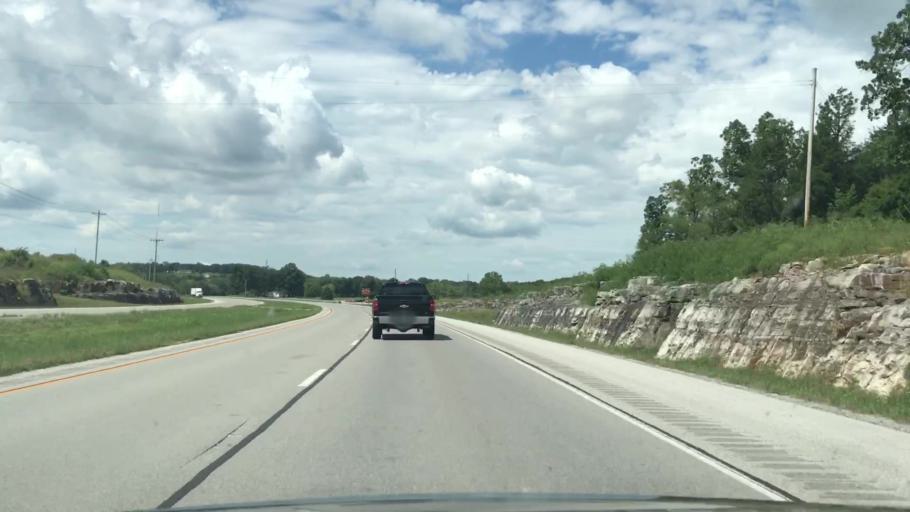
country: US
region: Kentucky
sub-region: Logan County
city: Russellville
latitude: 36.8670
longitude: -86.8922
